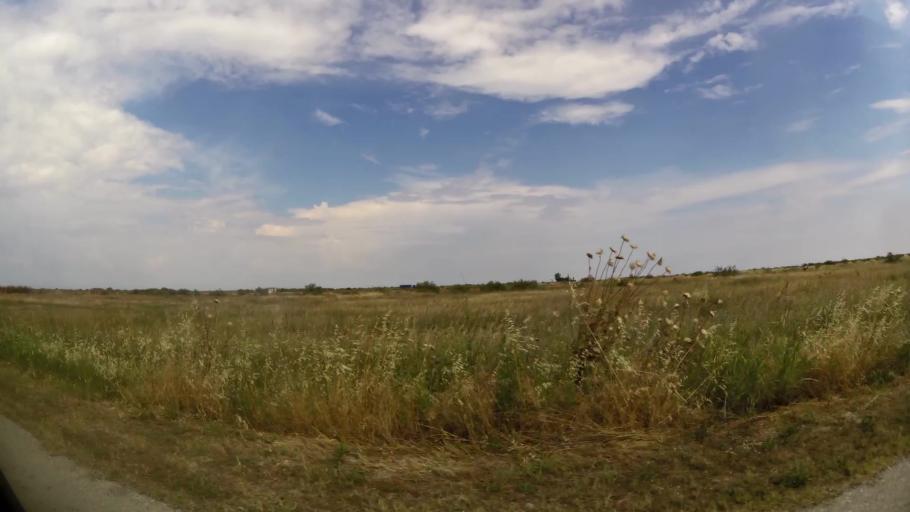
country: GR
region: Central Macedonia
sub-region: Nomos Pierias
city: Korinos
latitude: 40.3205
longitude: 22.6218
